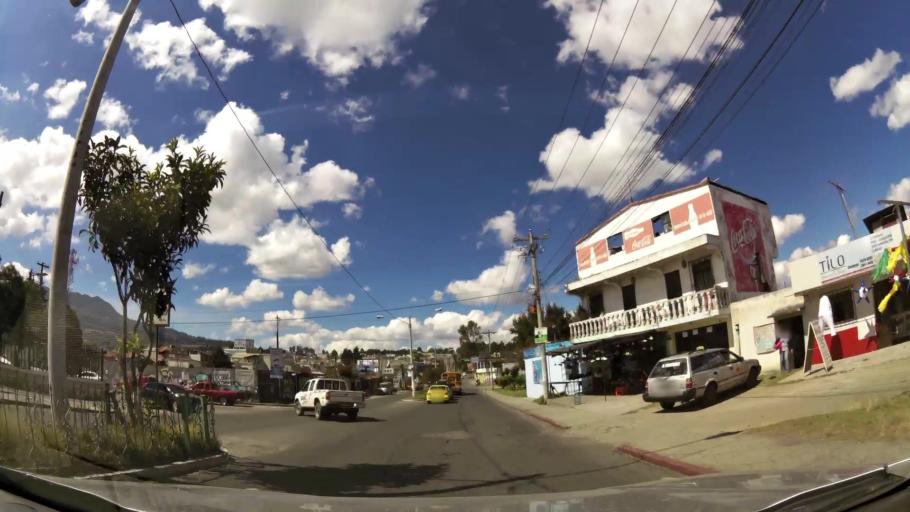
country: GT
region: Quetzaltenango
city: Quetzaltenango
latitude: 14.8418
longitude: -91.5276
